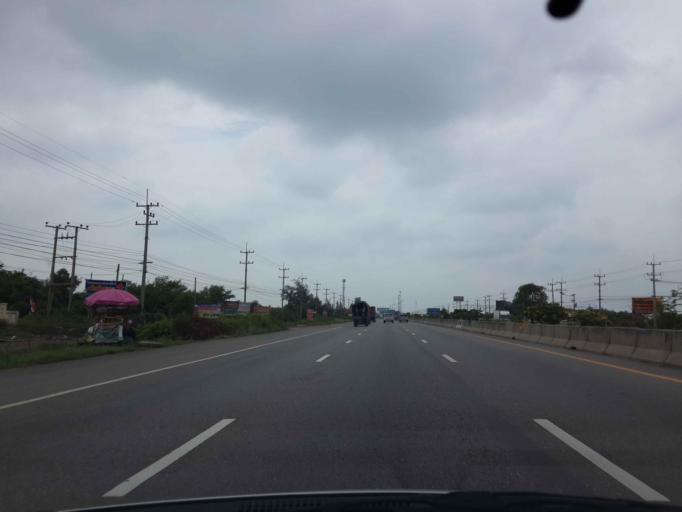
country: TH
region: Samut Songkhram
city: Samut Songkhram
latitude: 13.4556
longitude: 100.0886
